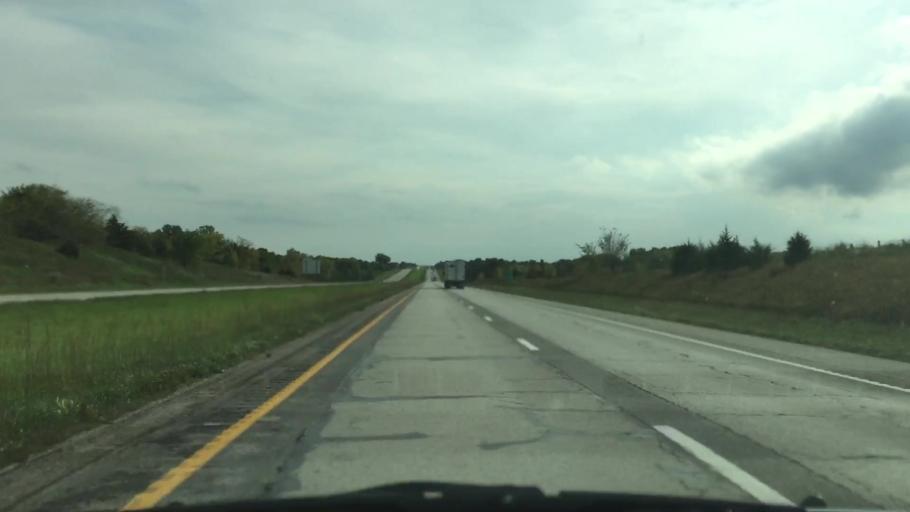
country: US
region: Iowa
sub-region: Decatur County
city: Lamoni
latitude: 40.4519
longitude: -93.9812
